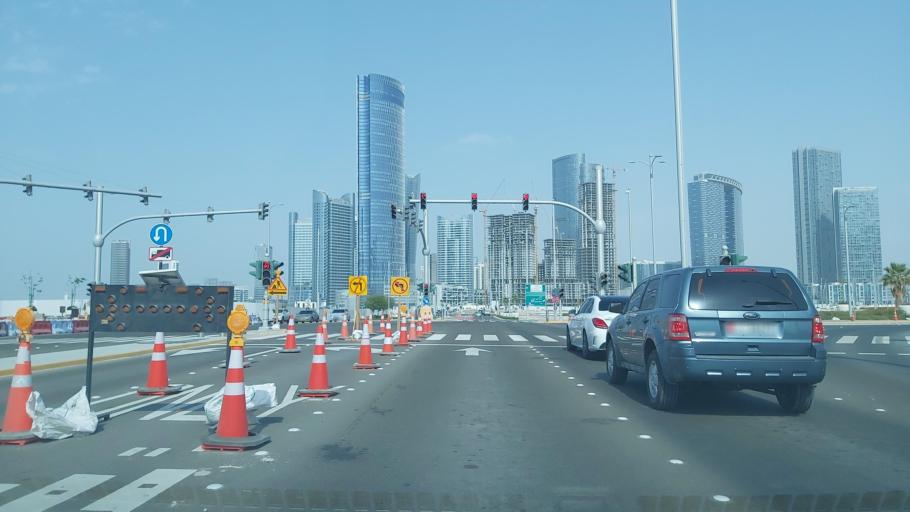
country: AE
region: Abu Dhabi
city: Abu Dhabi
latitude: 24.4983
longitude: 54.3950
